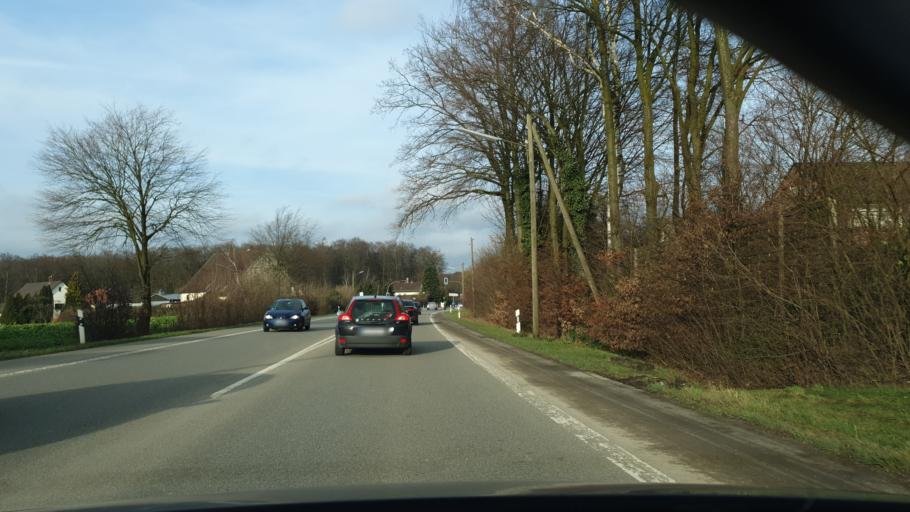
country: DE
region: North Rhine-Westphalia
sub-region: Regierungsbezirk Detmold
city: Bielefeld
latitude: 52.0787
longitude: 8.5156
